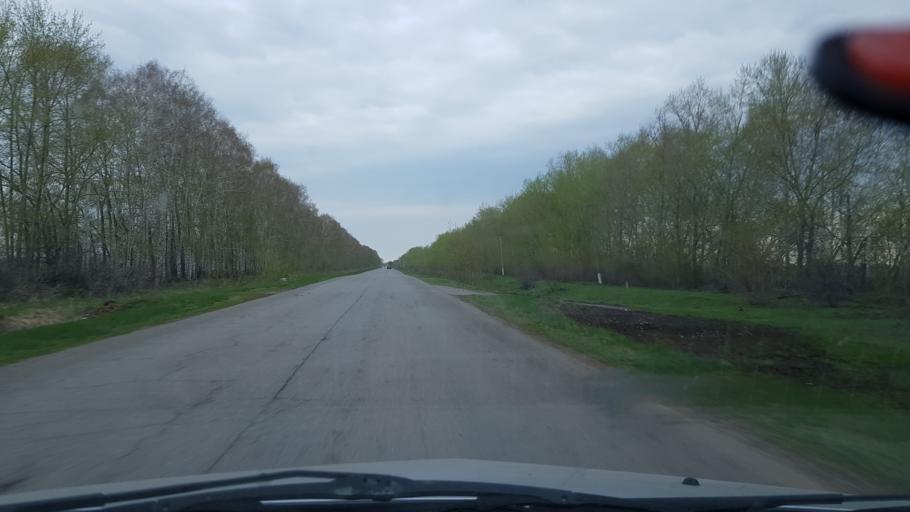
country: RU
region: Samara
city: Podstepki
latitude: 53.6626
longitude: 49.1980
